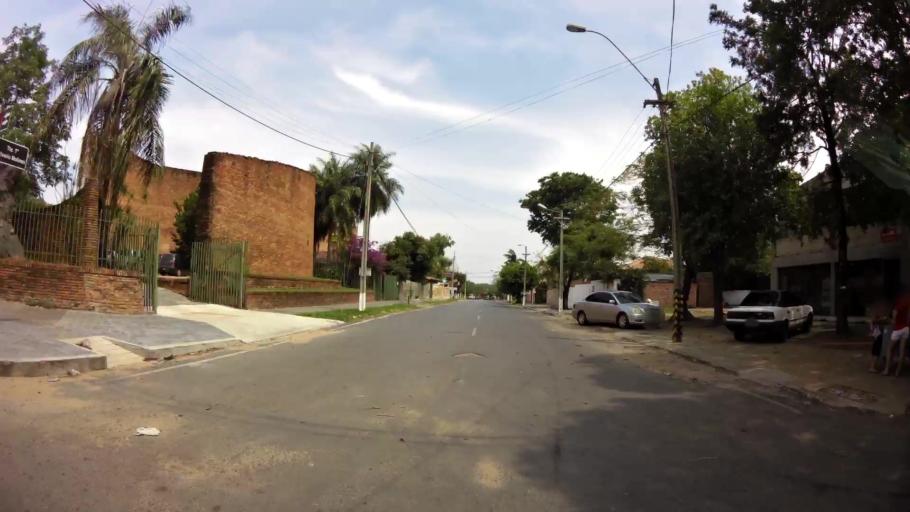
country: PY
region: Asuncion
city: Asuncion
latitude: -25.2639
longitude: -57.5820
